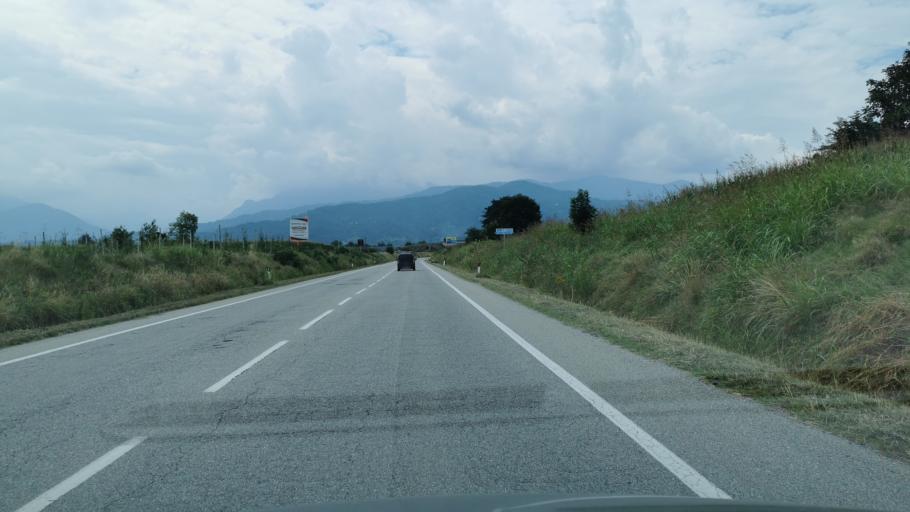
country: IT
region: Piedmont
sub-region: Provincia di Torino
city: Osasco
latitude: 44.8445
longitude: 7.3431
